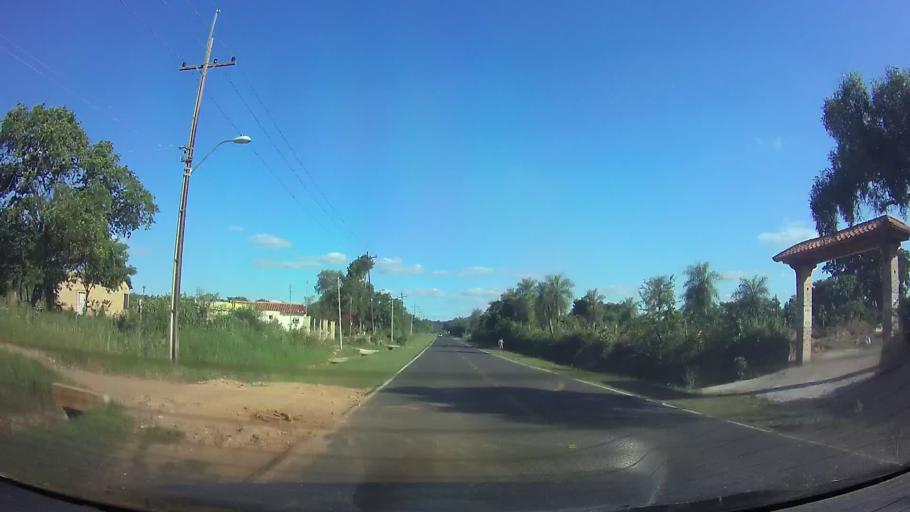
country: PY
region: Cordillera
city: Atyra
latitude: -25.2911
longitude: -57.1672
